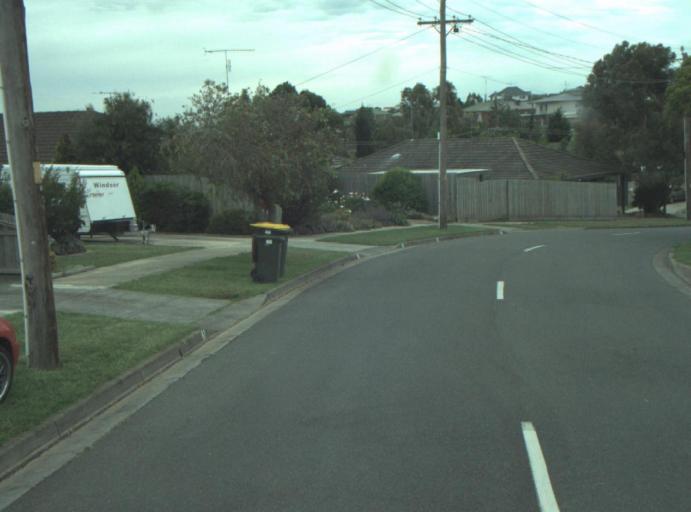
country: AU
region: Victoria
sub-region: Greater Geelong
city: Leopold
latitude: -38.1829
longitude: 144.4710
